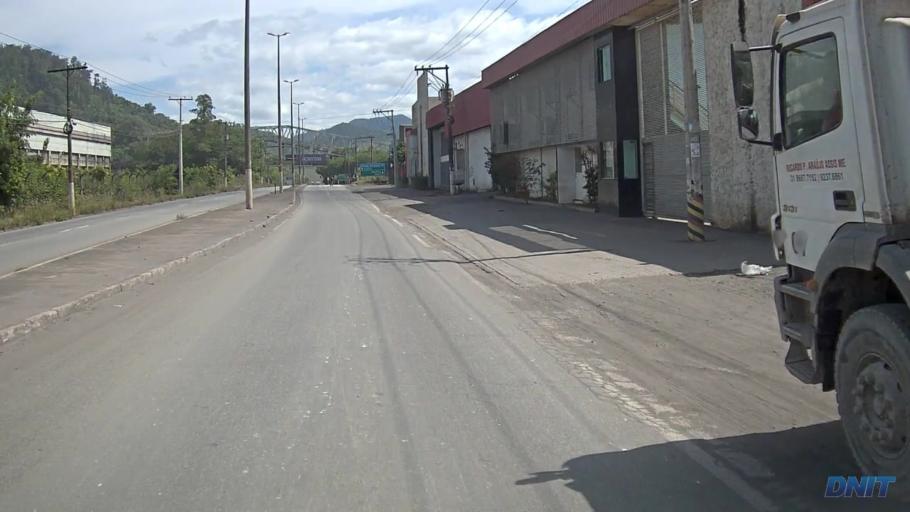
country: BR
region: Minas Gerais
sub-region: Coronel Fabriciano
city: Coronel Fabriciano
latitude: -19.5283
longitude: -42.6475
